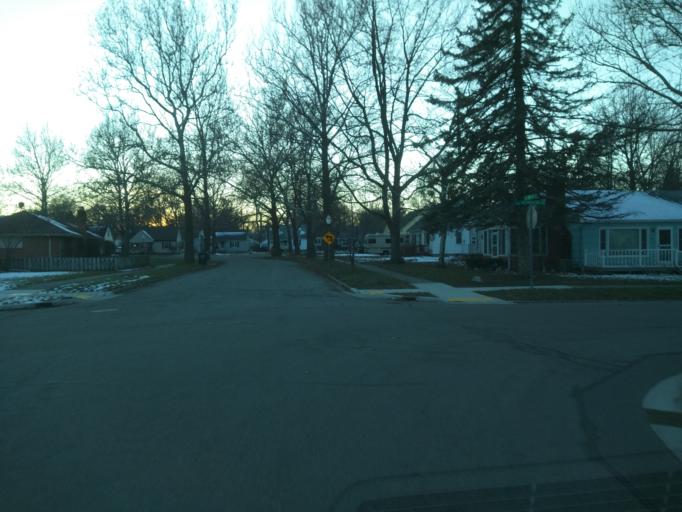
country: US
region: Michigan
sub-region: Ingham County
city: Lansing
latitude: 42.7003
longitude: -84.5391
